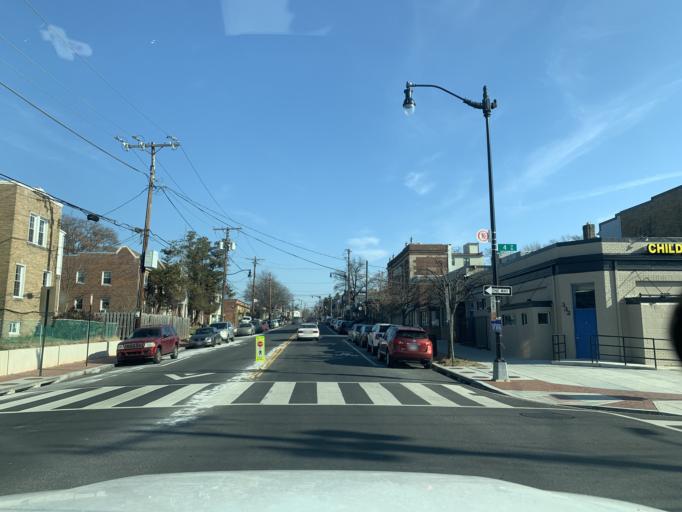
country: US
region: Maryland
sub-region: Montgomery County
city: Takoma Park
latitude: 38.9565
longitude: -77.0179
